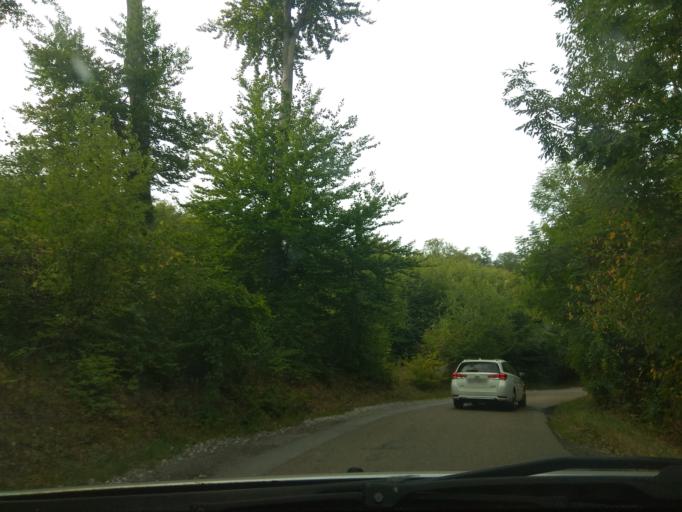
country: HU
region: Borsod-Abauj-Zemplen
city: Saly
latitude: 48.0645
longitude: 20.6739
